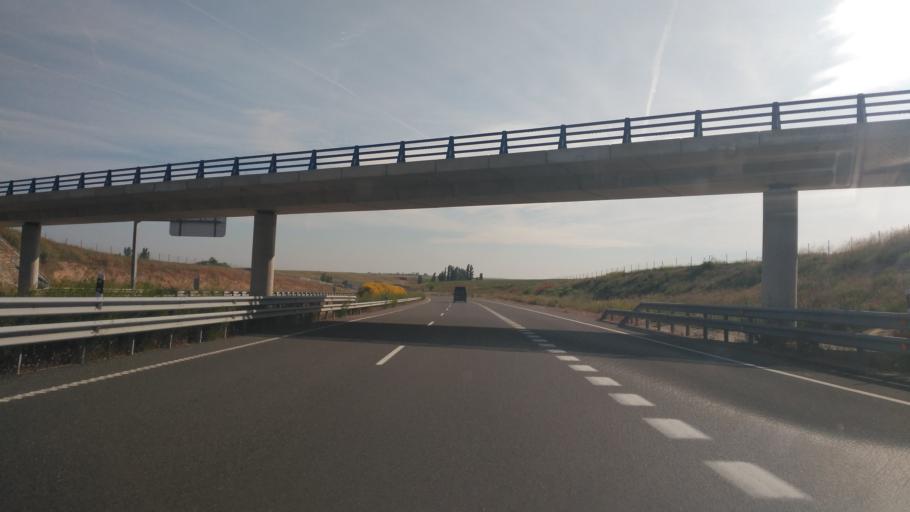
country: ES
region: Castille and Leon
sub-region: Provincia de Salamanca
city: Monterrubio de Armuna
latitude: 41.0327
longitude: -5.6717
